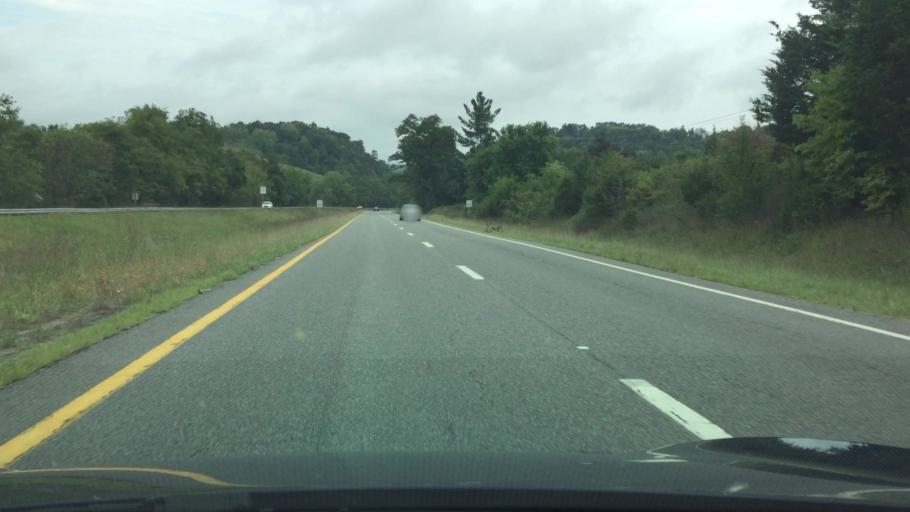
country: US
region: Virginia
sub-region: City of Radford
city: Radford
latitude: 37.1032
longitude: -80.5179
